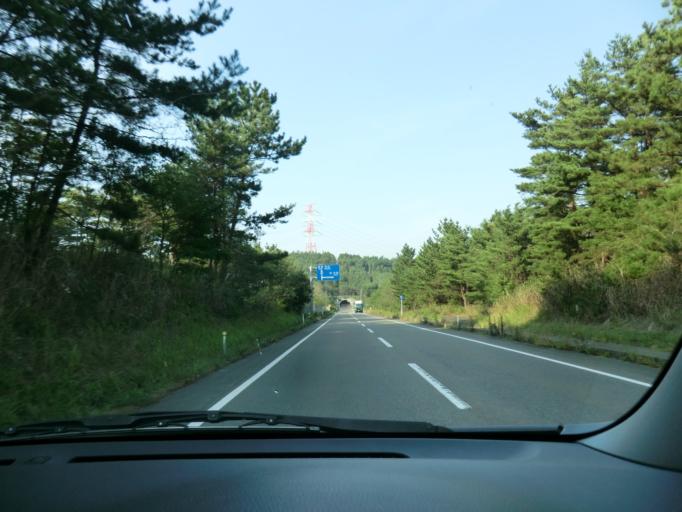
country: JP
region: Niigata
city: Kashiwazaki
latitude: 37.4334
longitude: 138.6115
